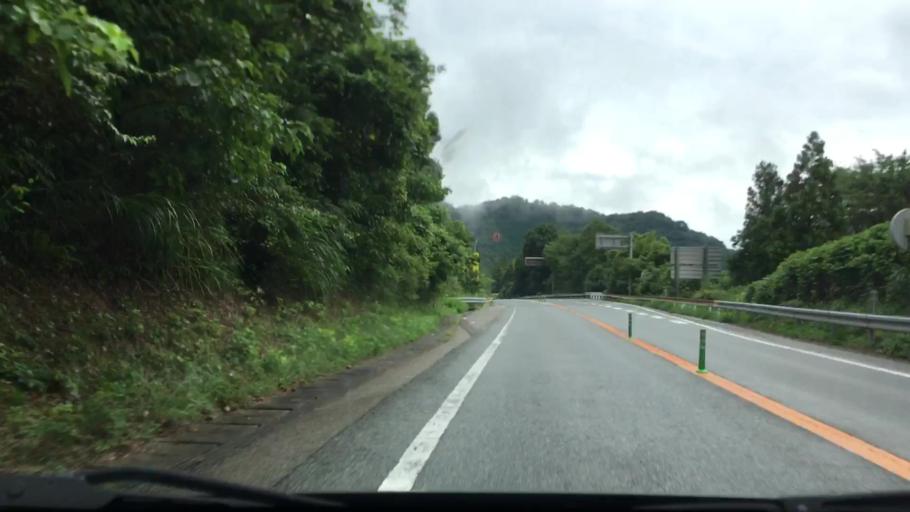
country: JP
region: Hyogo
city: Nishiwaki
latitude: 35.0220
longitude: 134.7663
